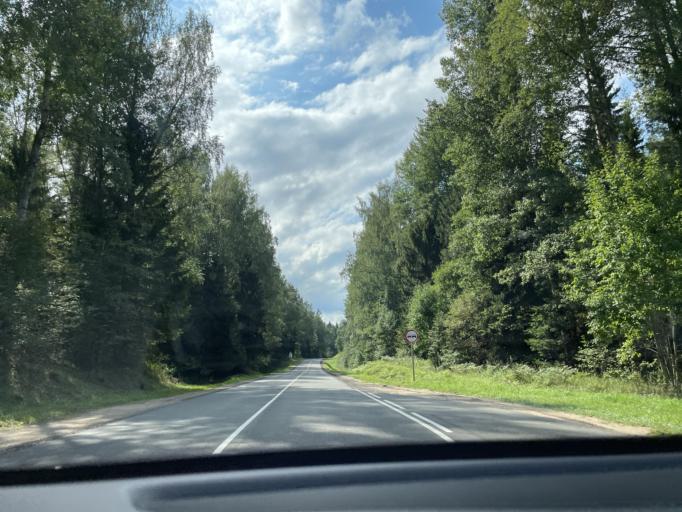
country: RU
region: Novgorod
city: Valday
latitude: 58.0329
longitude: 33.2155
